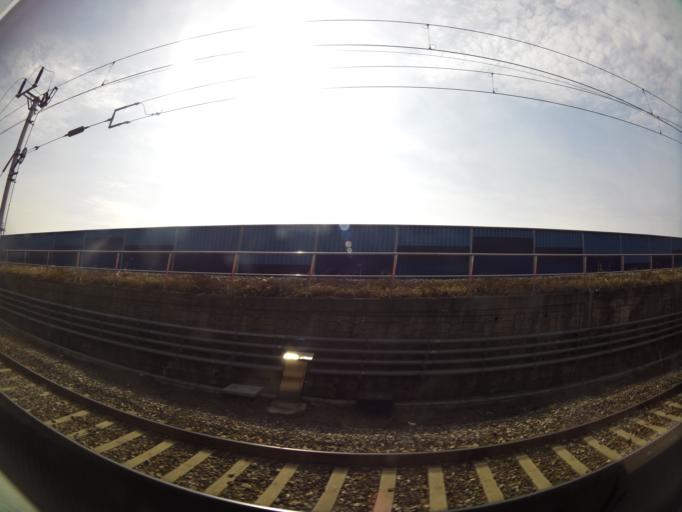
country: KR
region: Daejeon
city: Songgang-dong
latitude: 36.5339
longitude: 127.3583
